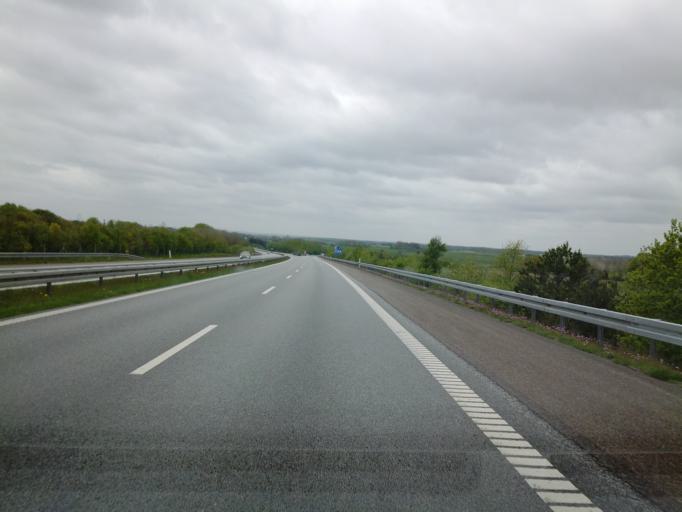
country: DK
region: North Denmark
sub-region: Frederikshavn Kommune
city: Saeby
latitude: 57.3536
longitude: 10.4653
